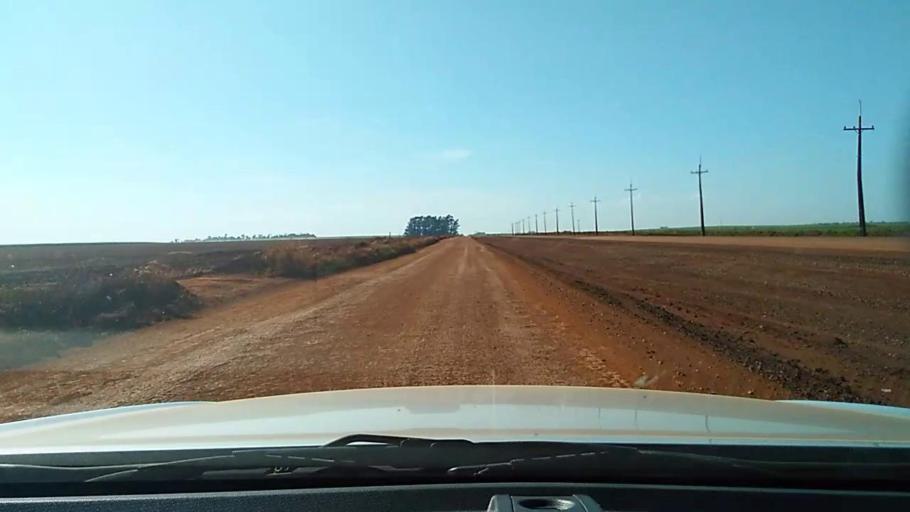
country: PY
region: Alto Parana
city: Naranjal
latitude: -25.9170
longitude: -55.4333
